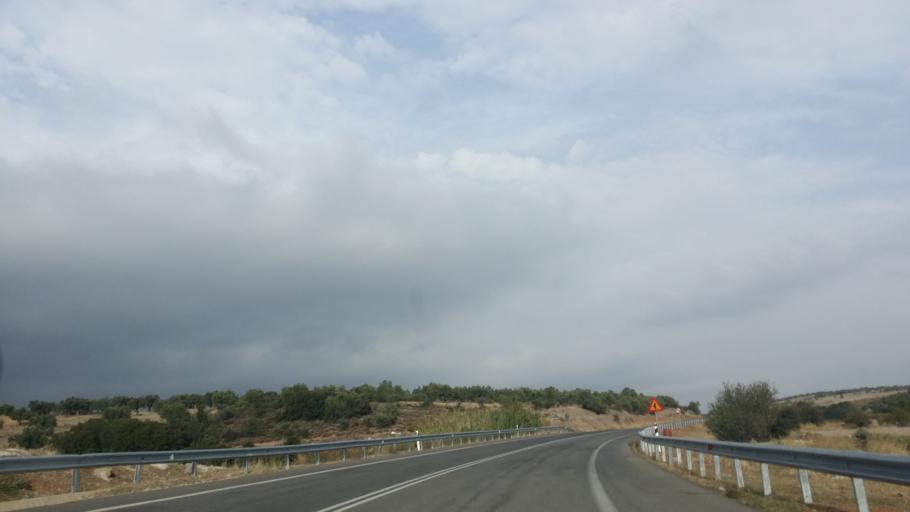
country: GR
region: Central Greece
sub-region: Nomos Voiotias
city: Thespies
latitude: 38.2722
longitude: 23.0929
